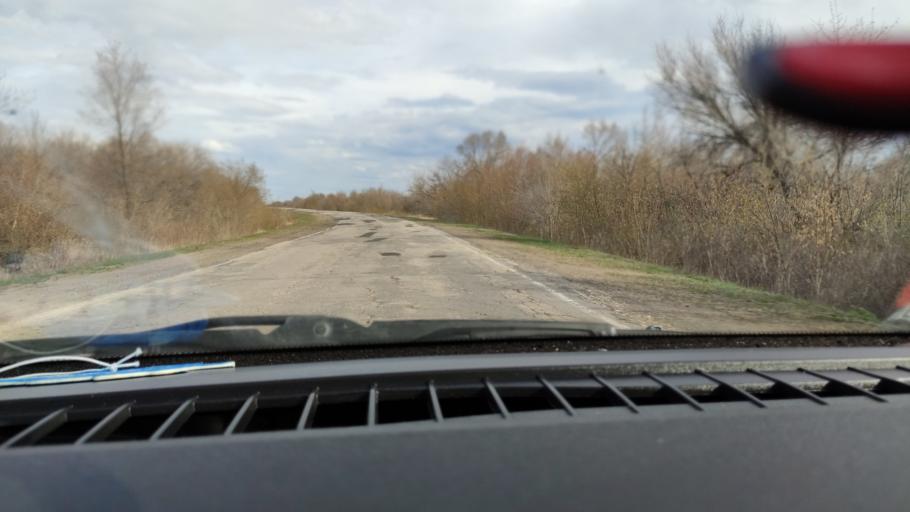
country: RU
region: Saratov
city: Rovnoye
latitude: 51.0697
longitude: 45.9928
